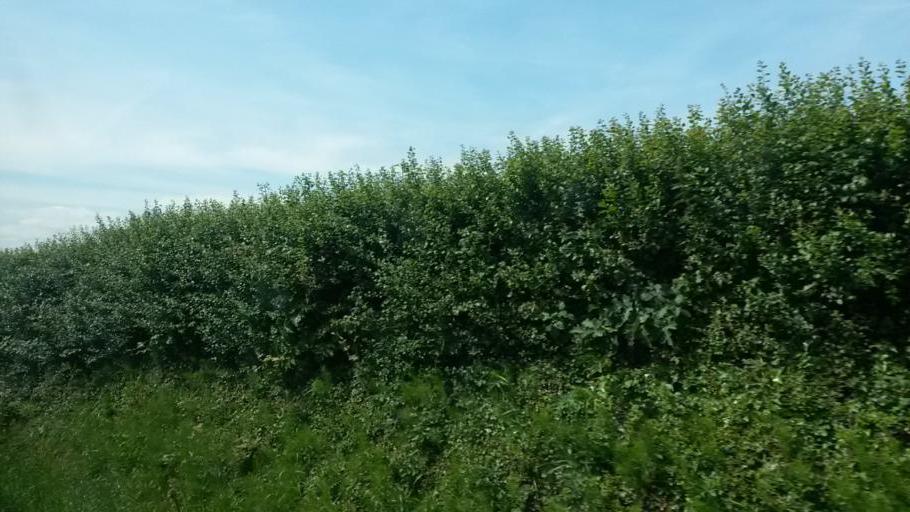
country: IE
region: Leinster
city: Lusk
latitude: 53.5381
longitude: -6.1936
